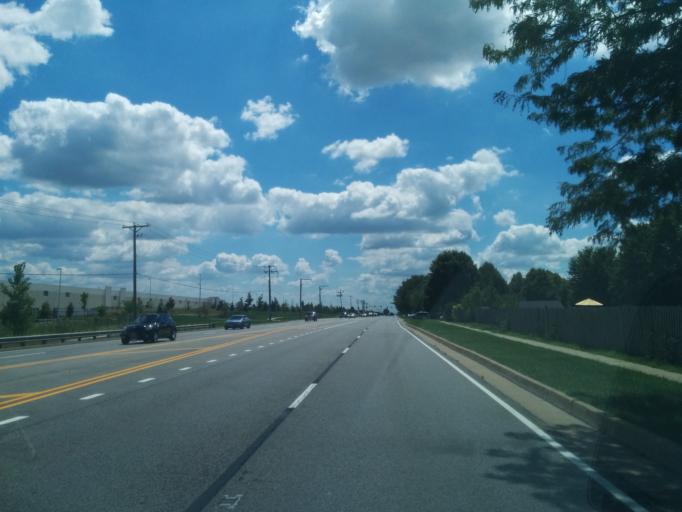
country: US
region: Illinois
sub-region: Will County
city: Romeoville
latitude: 41.6796
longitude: -88.1257
